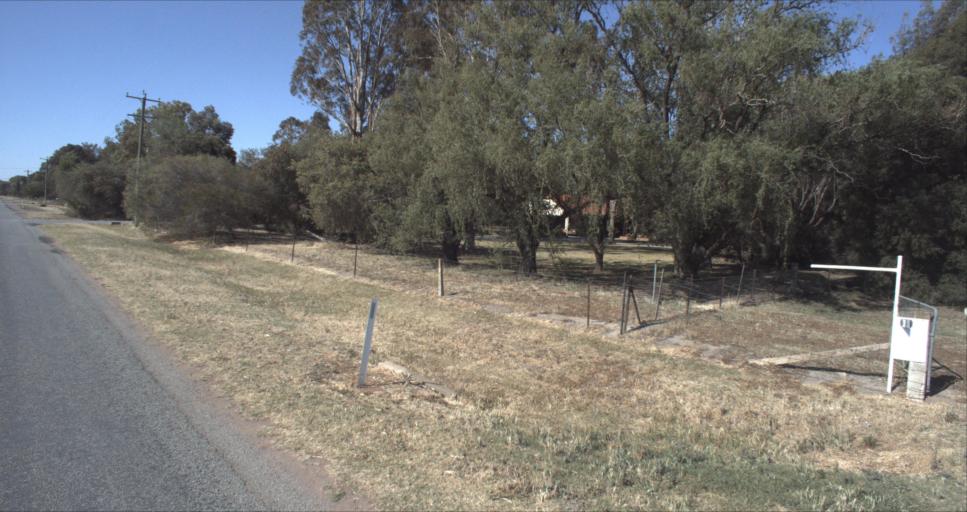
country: AU
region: New South Wales
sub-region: Leeton
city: Leeton
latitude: -34.5425
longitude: 146.4188
